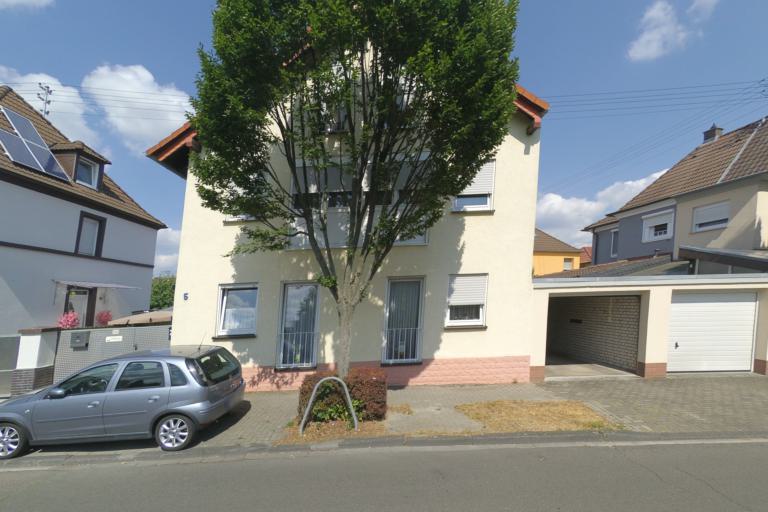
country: DE
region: Rheinland-Pfalz
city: Frankenthal
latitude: 49.5171
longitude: 8.3976
